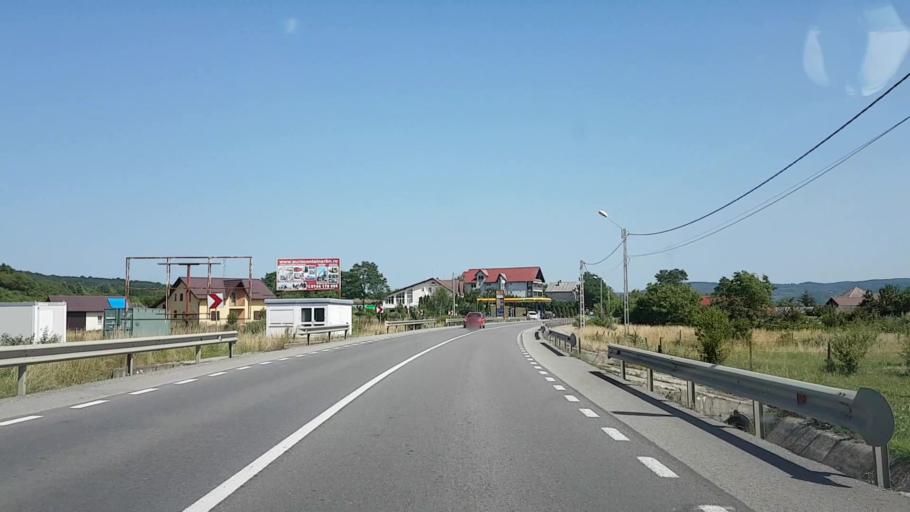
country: RO
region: Bistrita-Nasaud
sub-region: Comuna Uriu
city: Cristestii Ciceului
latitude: 47.1820
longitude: 24.1373
